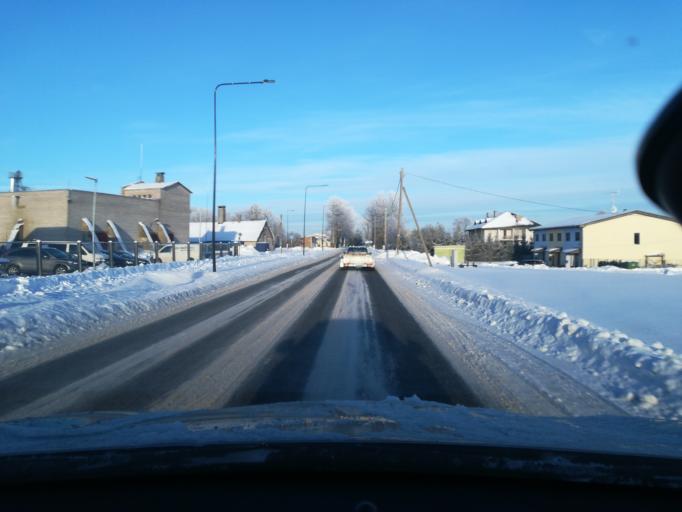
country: EE
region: Harju
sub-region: Saue linn
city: Saue
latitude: 59.3407
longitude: 24.5551
